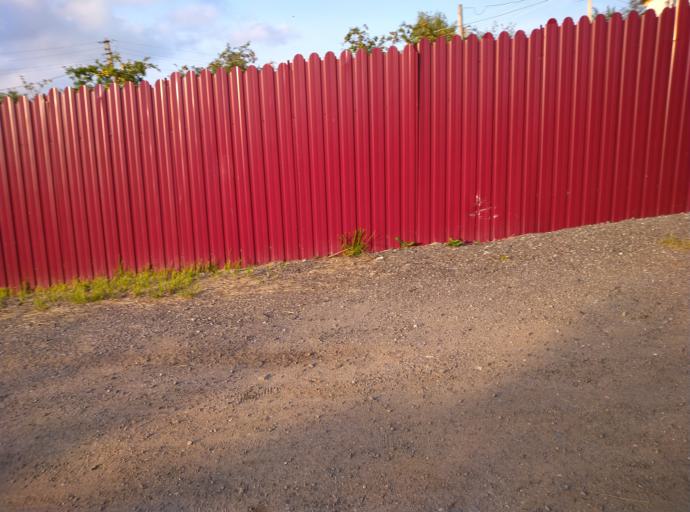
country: RU
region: Kostroma
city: Oktyabr'skiy
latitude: 57.7518
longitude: 40.9652
